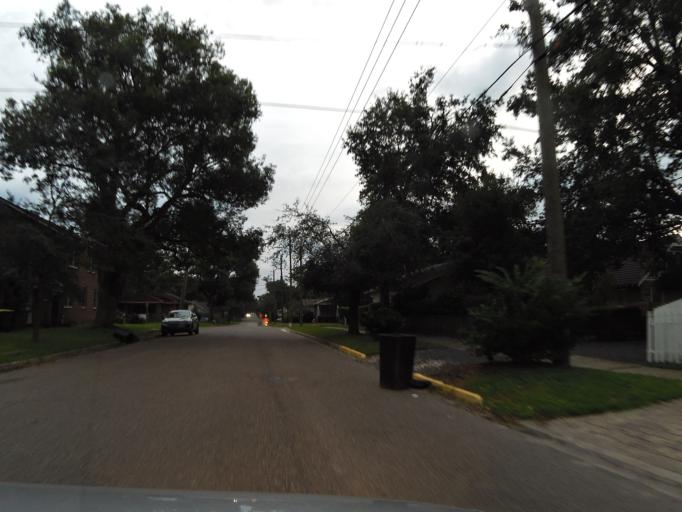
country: US
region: Florida
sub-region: Duval County
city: Jacksonville
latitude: 30.2998
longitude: -81.7102
